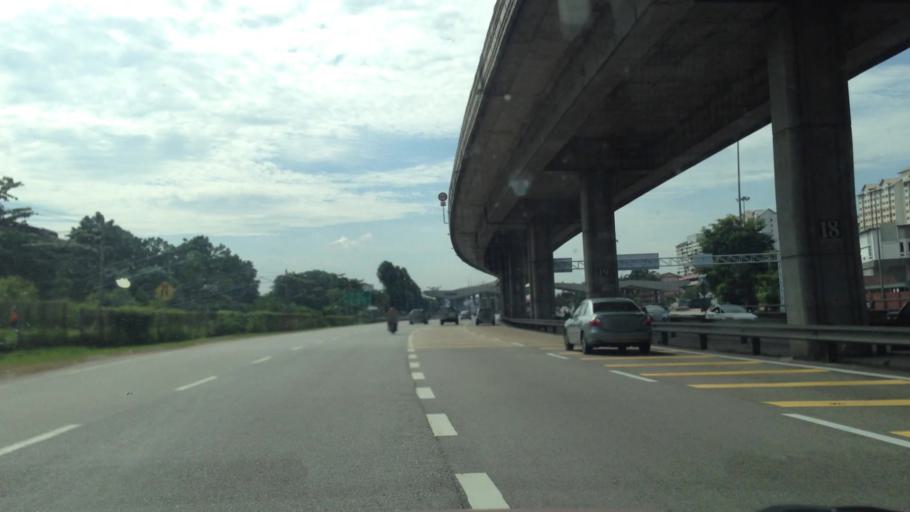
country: MY
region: Selangor
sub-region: Petaling
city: Petaling Jaya
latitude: 3.0848
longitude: 101.6285
